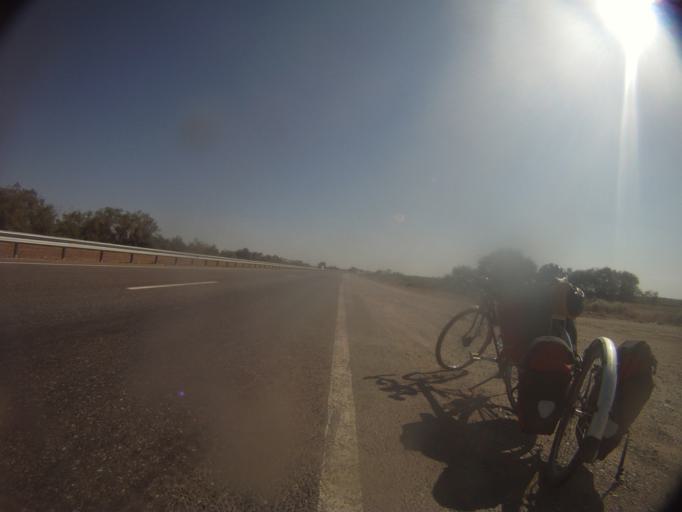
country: KZ
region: Zhambyl
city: Taraz
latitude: 42.7397
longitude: 70.9823
